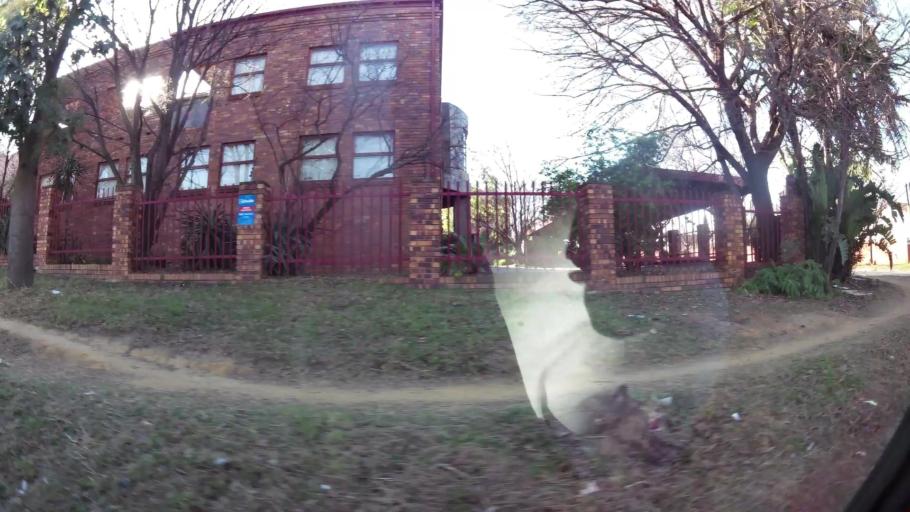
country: ZA
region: Gauteng
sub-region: City of Johannesburg Metropolitan Municipality
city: Roodepoort
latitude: -26.0876
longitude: 27.9618
